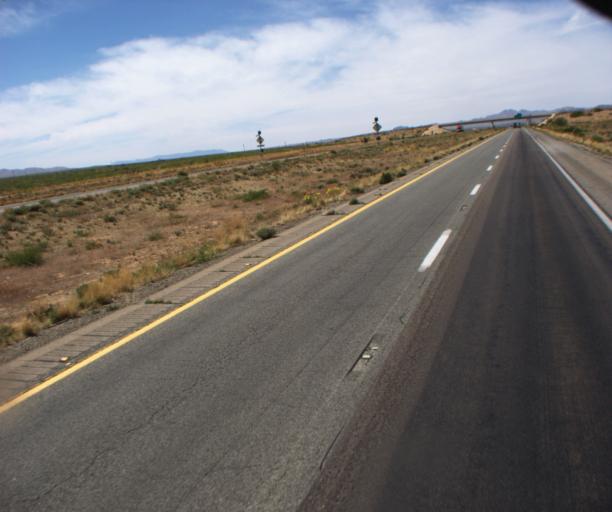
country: US
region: Arizona
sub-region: Cochise County
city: Willcox
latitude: 32.3270
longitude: -109.5087
